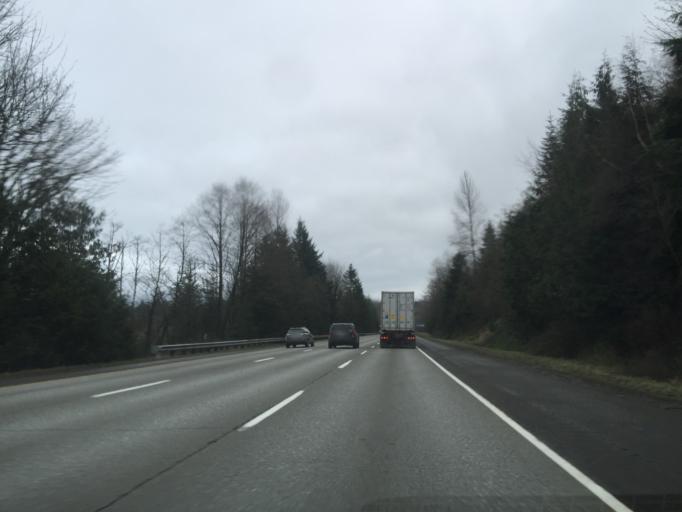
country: US
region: Washington
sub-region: King County
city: North Bend
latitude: 47.4984
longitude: -121.8173
